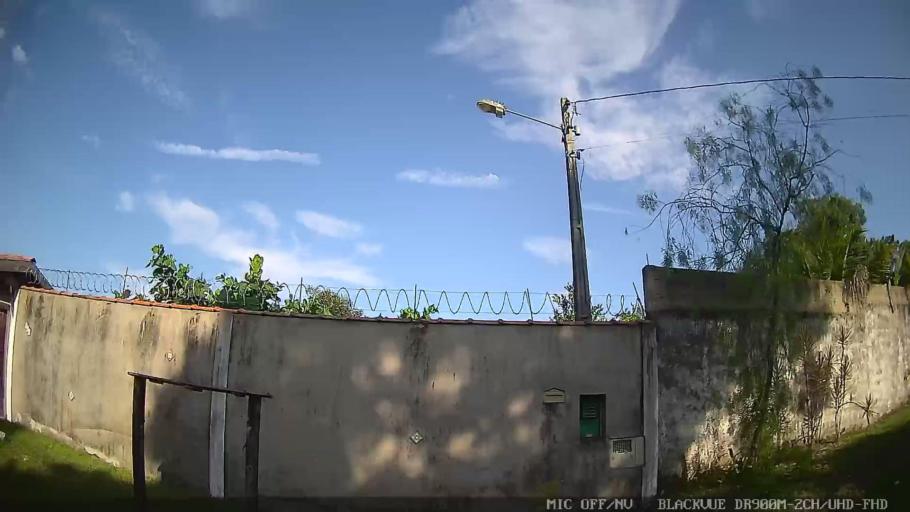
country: BR
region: Sao Paulo
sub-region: Itanhaem
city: Itanhaem
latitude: -24.1717
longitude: -46.8209
